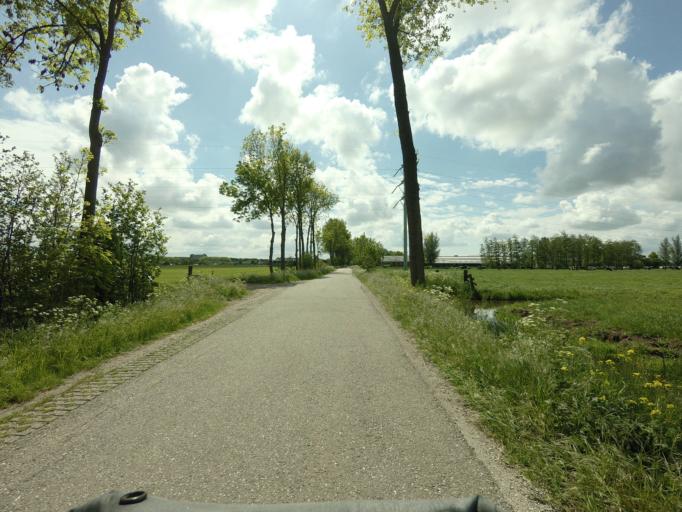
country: NL
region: South Holland
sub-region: Gemeente Gorinchem
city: Gorinchem
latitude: 51.8550
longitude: 4.9410
